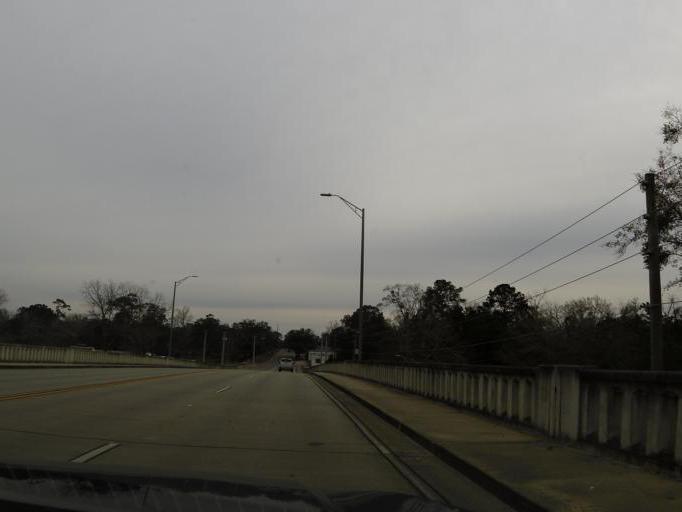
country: US
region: Georgia
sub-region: Thomas County
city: Thomasville
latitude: 30.8467
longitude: -83.9902
